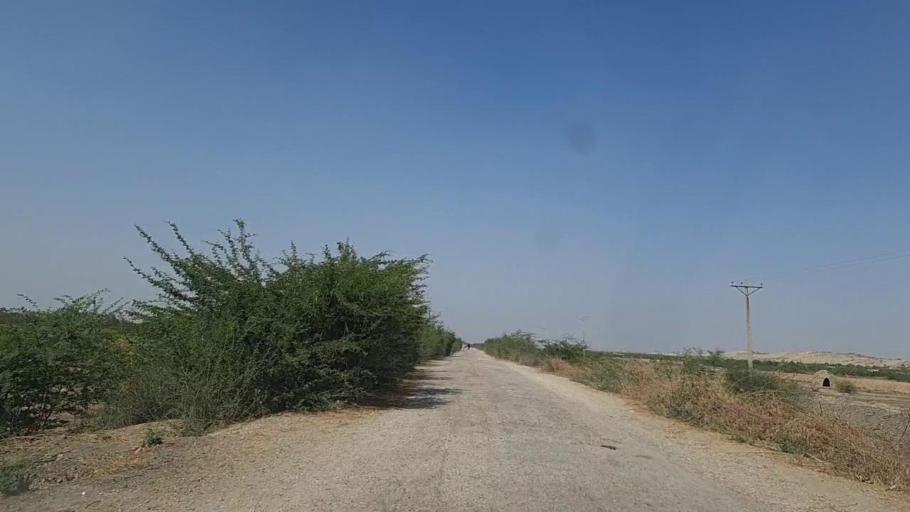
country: PK
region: Sindh
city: Naukot
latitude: 24.6249
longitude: 69.2890
